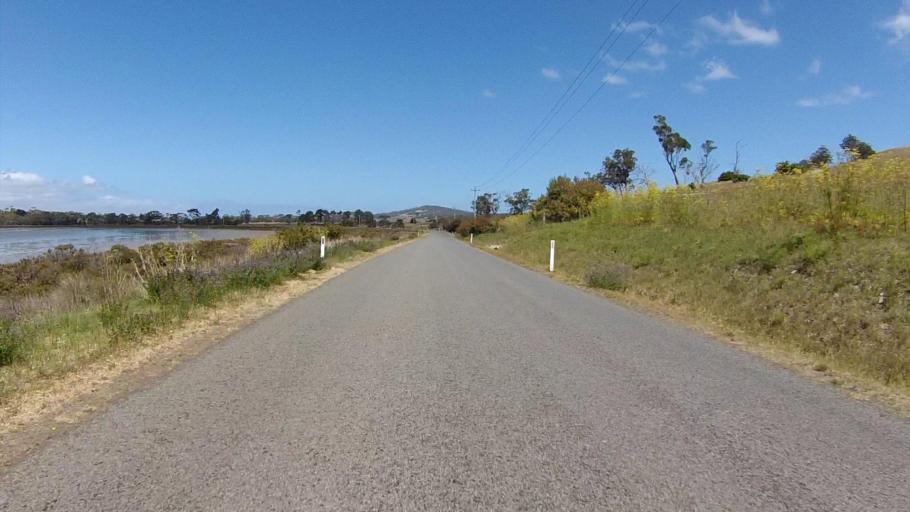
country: AU
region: Tasmania
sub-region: Clarence
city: Lauderdale
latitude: -42.9253
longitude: 147.4818
